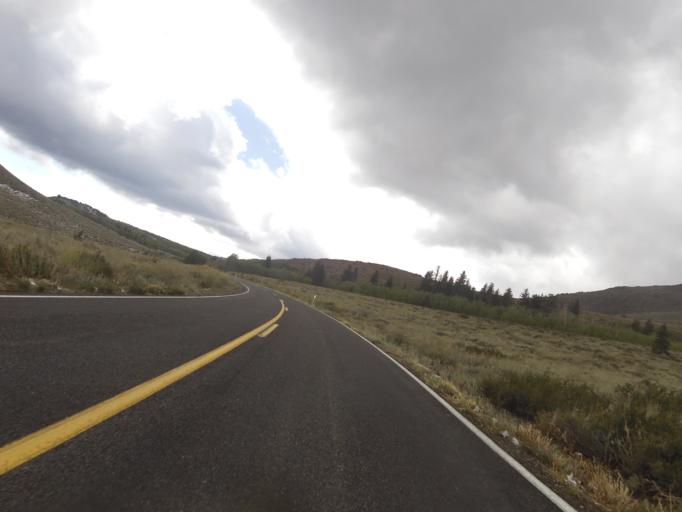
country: US
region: Nevada
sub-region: Douglas County
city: Gardnerville Ranchos
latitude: 38.6809
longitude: -119.5977
